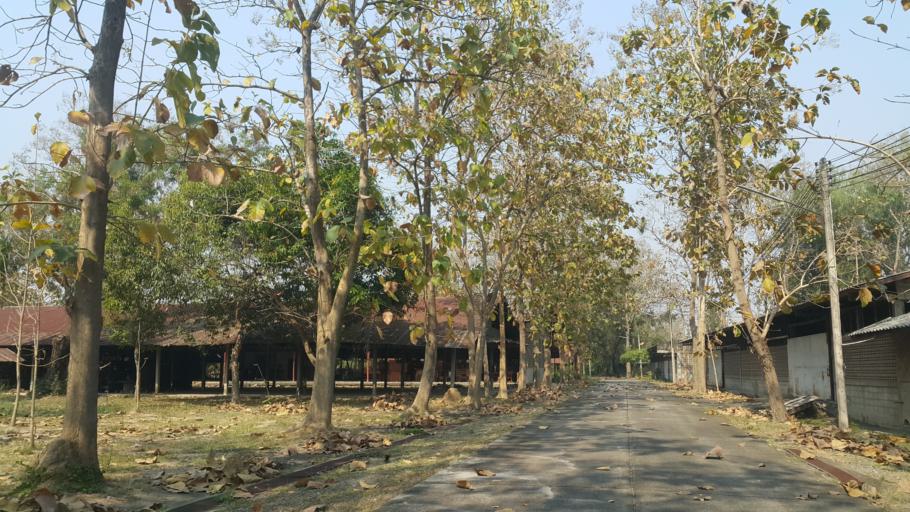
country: TH
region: Chiang Mai
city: San Kamphaeng
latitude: 18.7697
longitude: 99.0774
